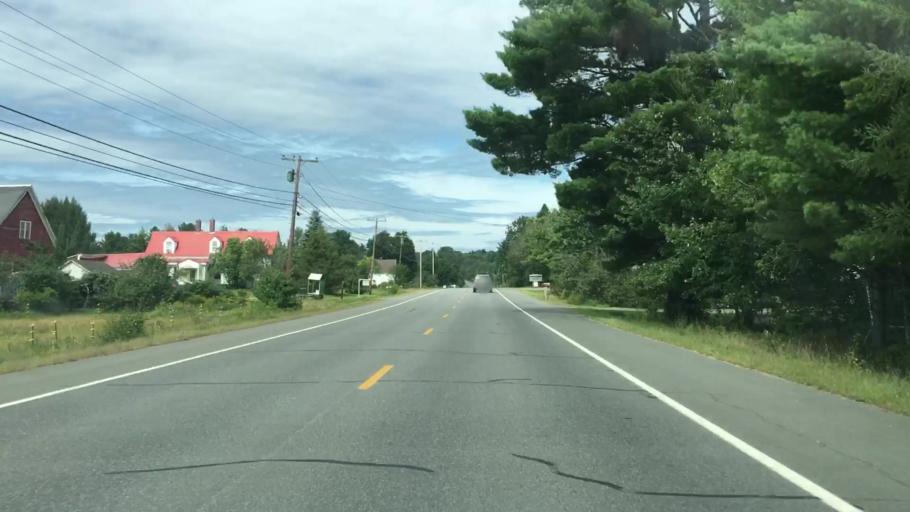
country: US
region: Maine
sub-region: Piscataquis County
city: Milo
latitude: 45.2711
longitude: -68.9988
